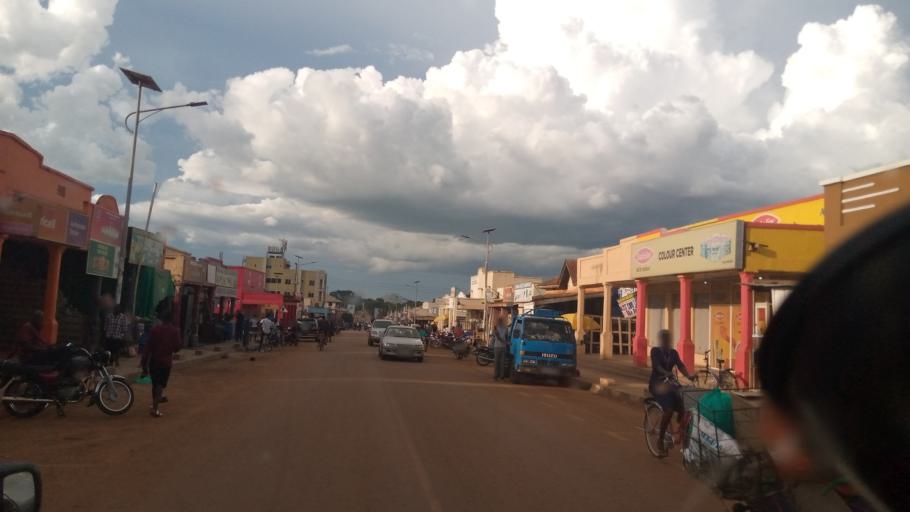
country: UG
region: Northern Region
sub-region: Lira District
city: Lira
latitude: 2.2403
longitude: 32.8953
